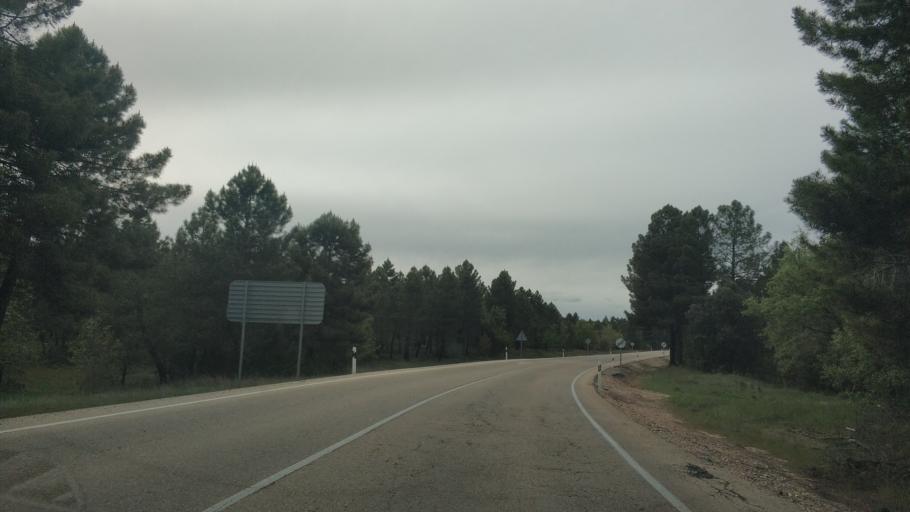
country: ES
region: Castille and Leon
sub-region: Provincia de Soria
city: Bayubas de Abajo
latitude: 41.5129
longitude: -2.9256
